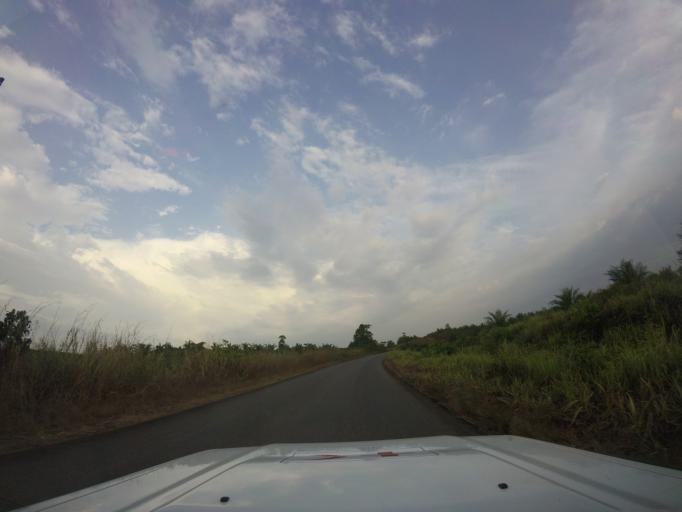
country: LR
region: Bomi
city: Tubmanburg
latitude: 6.7129
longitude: -10.9384
